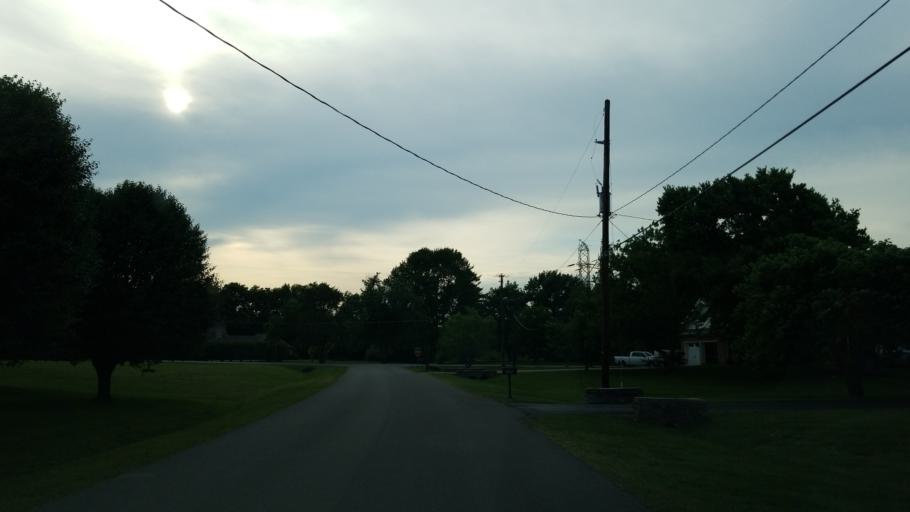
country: US
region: Tennessee
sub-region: Davidson County
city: Forest Hills
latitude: 36.0416
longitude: -86.8570
